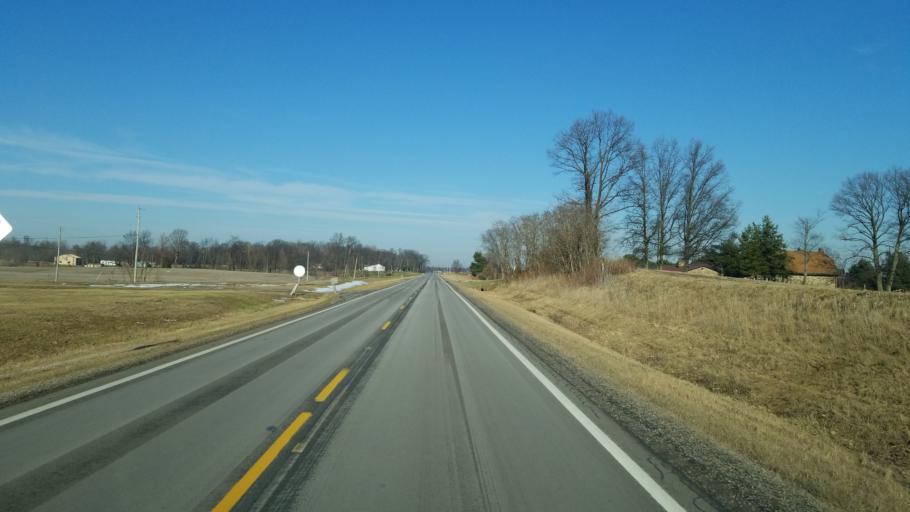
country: US
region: Ohio
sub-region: Huron County
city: Norwalk
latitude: 41.1829
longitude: -82.6392
